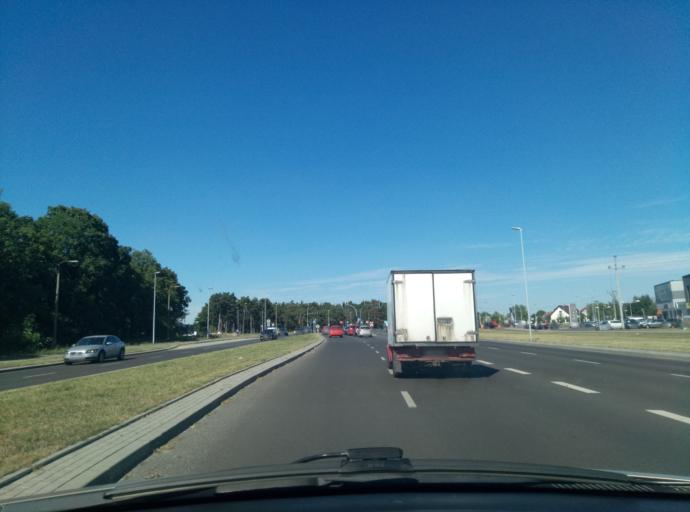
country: PL
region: Kujawsko-Pomorskie
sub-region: Torun
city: Torun
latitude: 53.0387
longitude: 18.5987
